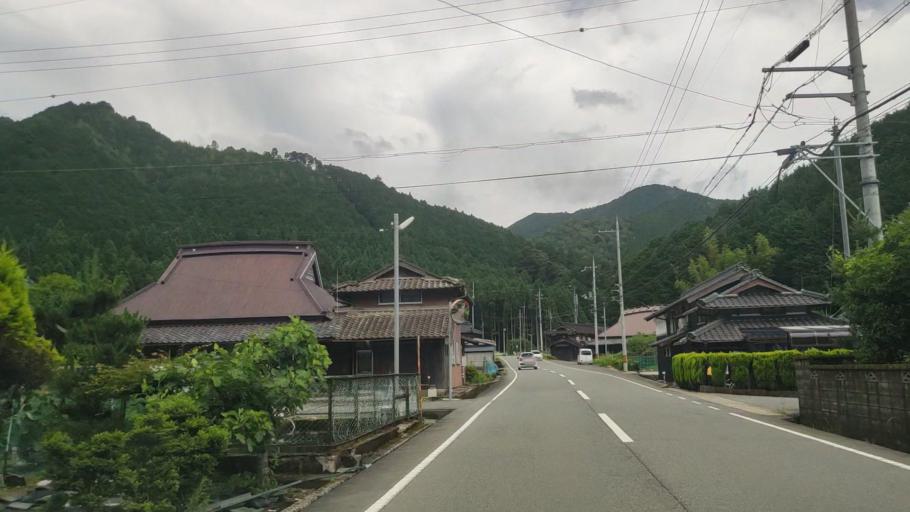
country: JP
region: Hyogo
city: Nishiwaki
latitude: 35.1863
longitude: 134.9304
